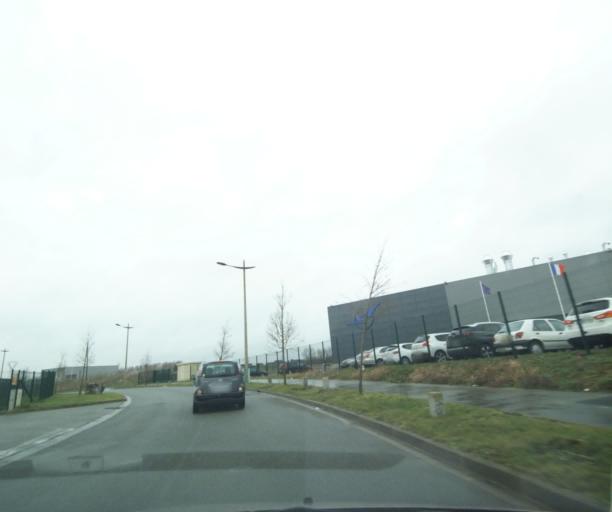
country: FR
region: Nord-Pas-de-Calais
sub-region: Departement du Nord
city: Herin
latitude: 50.3411
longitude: 3.4511
